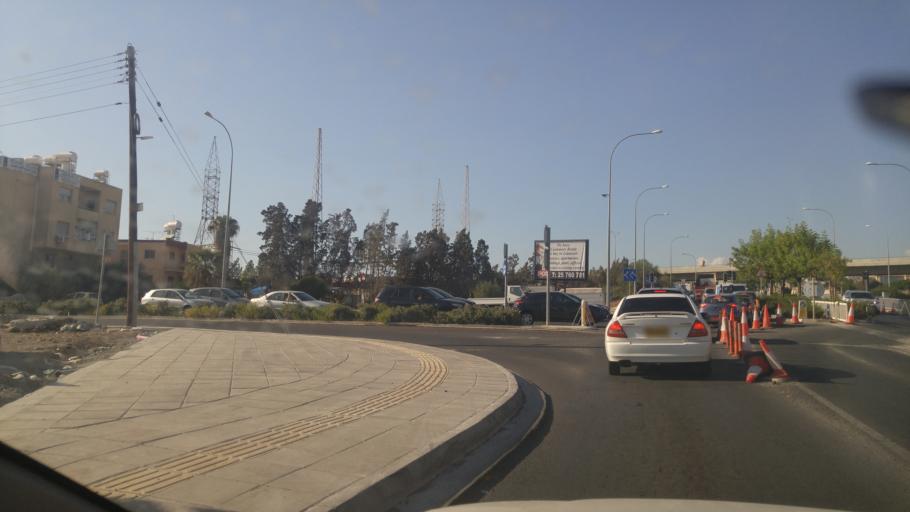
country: CY
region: Limassol
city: Limassol
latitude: 34.7030
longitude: 33.0277
